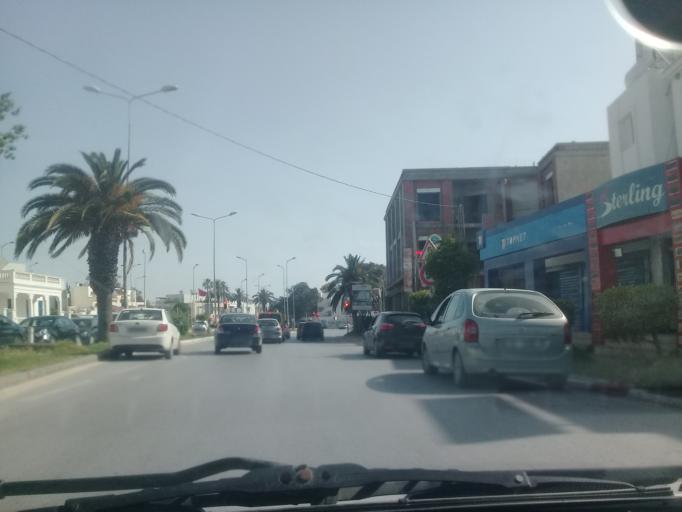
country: TN
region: Tunis
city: Al Marsa
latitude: 36.8777
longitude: 10.3268
